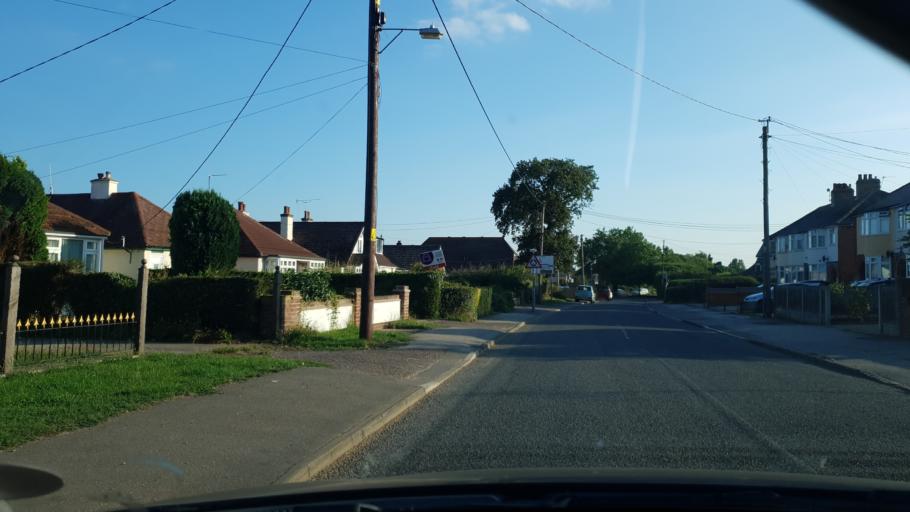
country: GB
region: England
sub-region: Essex
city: Frinton-on-Sea
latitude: 51.8433
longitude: 1.2206
